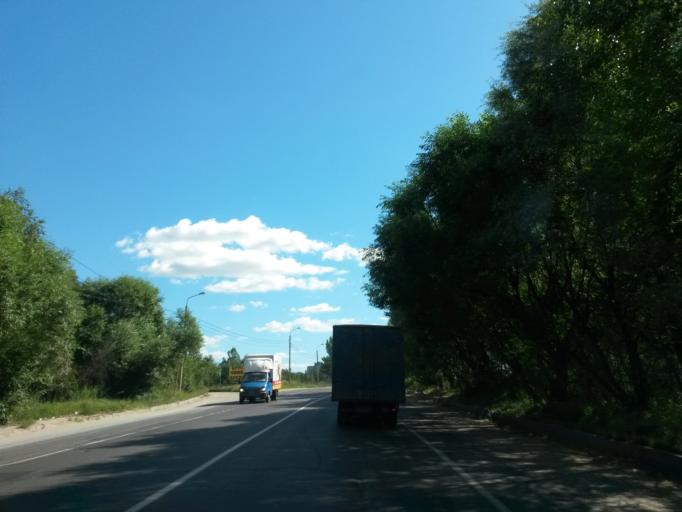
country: RU
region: Jaroslavl
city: Yaroslavl
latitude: 57.5908
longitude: 39.8168
